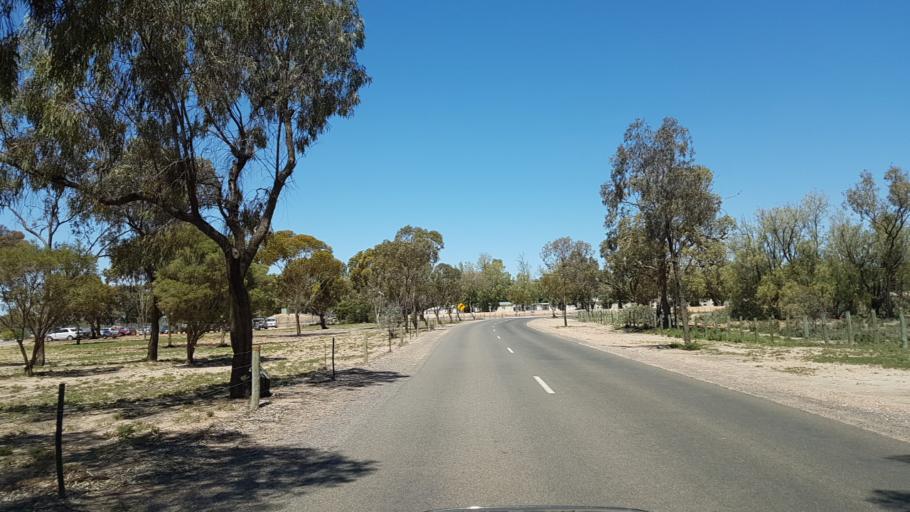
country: AU
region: South Australia
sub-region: Loxton Waikerie
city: Waikerie
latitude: -34.1723
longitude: 139.9804
